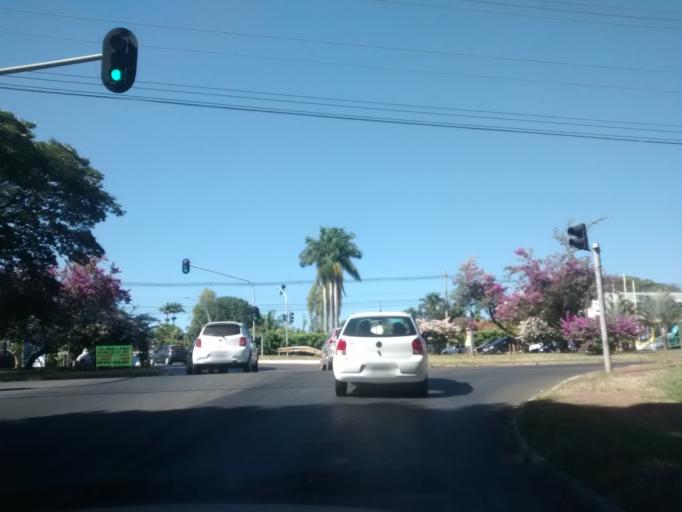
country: BR
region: Federal District
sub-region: Brasilia
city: Brasilia
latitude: -15.8454
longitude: -47.8966
